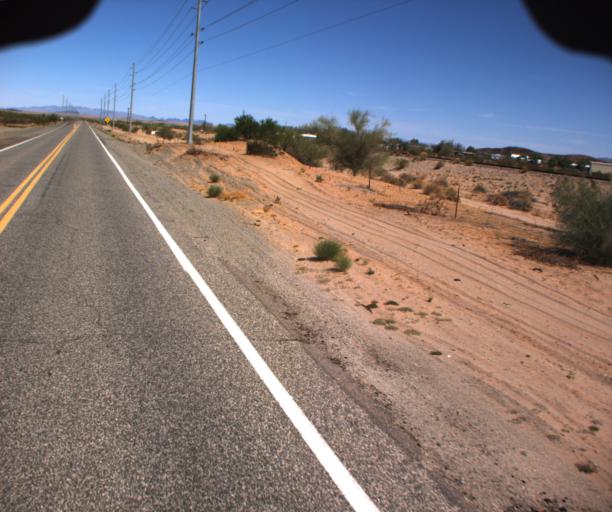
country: US
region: Arizona
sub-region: La Paz County
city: Cienega Springs
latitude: 33.9580
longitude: -114.0289
